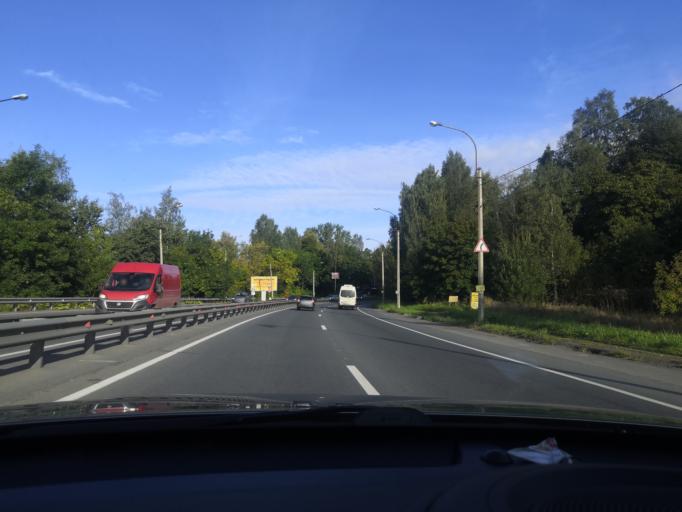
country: RU
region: St.-Petersburg
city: Pargolovo
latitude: 60.0796
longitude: 30.2653
